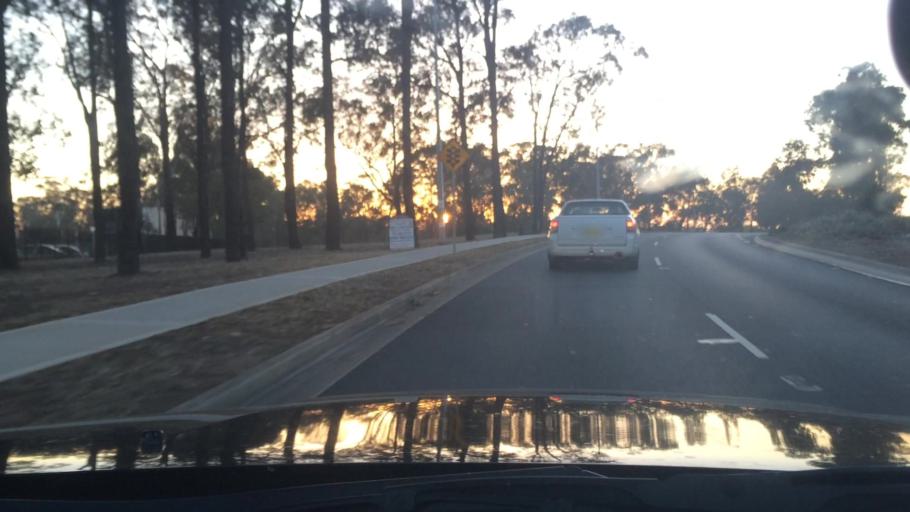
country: AU
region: New South Wales
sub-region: Fairfield
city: Fairfield Heights
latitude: -33.8494
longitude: 150.9041
